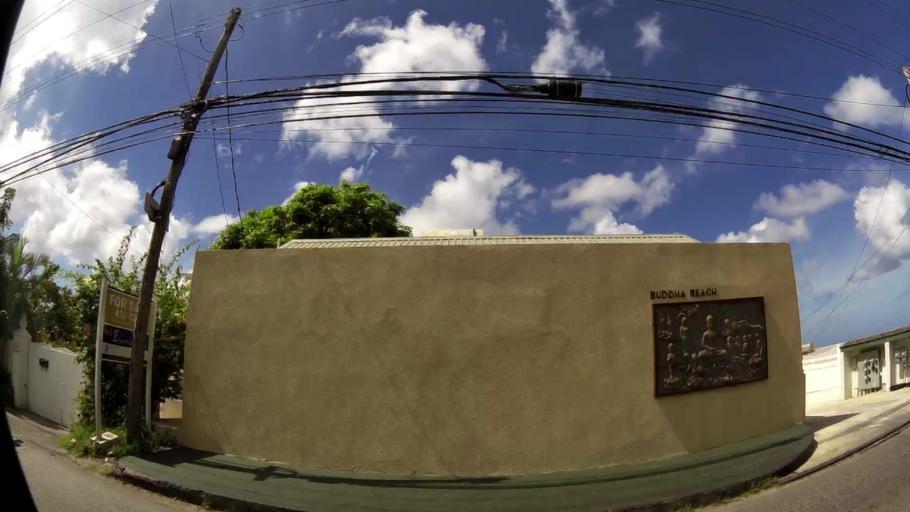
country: BB
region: Saint Michael
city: Bridgetown
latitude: 13.1386
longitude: -59.6367
